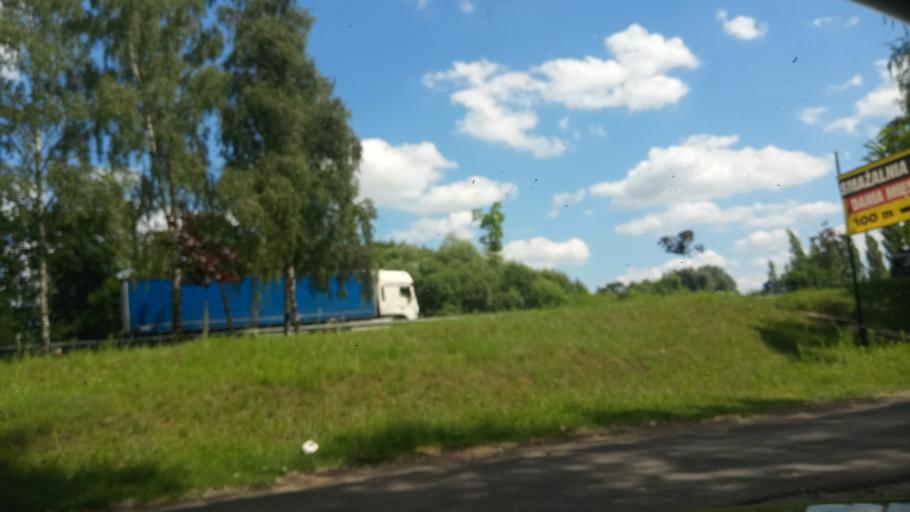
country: PL
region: Kujawsko-Pomorskie
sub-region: Powiat lipnowski
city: Kikol
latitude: 52.9074
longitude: 19.1198
